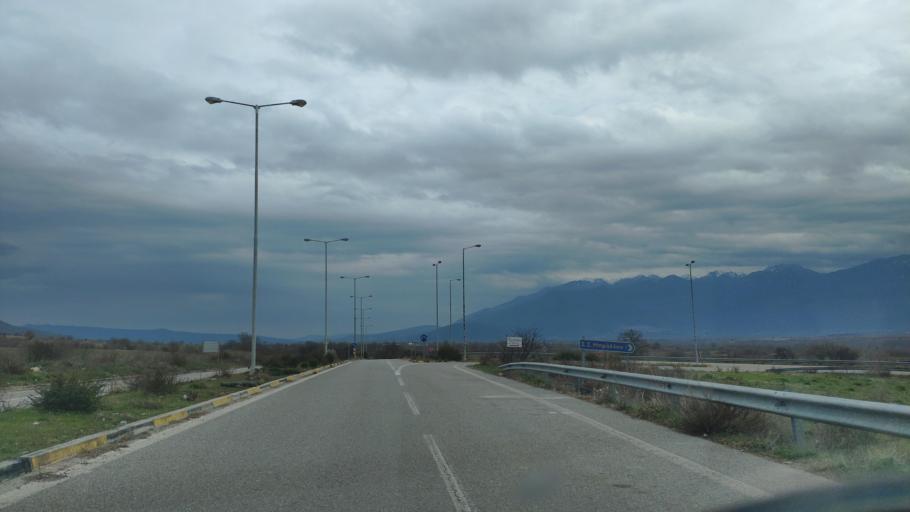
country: GR
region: Central Greece
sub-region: Nomos Fthiotidos
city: Anthili
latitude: 38.7129
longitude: 22.4605
